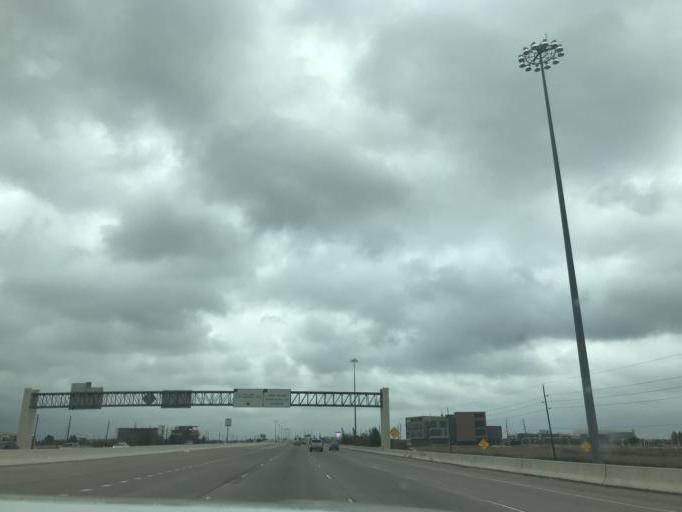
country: US
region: Texas
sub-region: Fort Bend County
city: Greatwood
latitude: 29.5755
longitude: -95.6563
